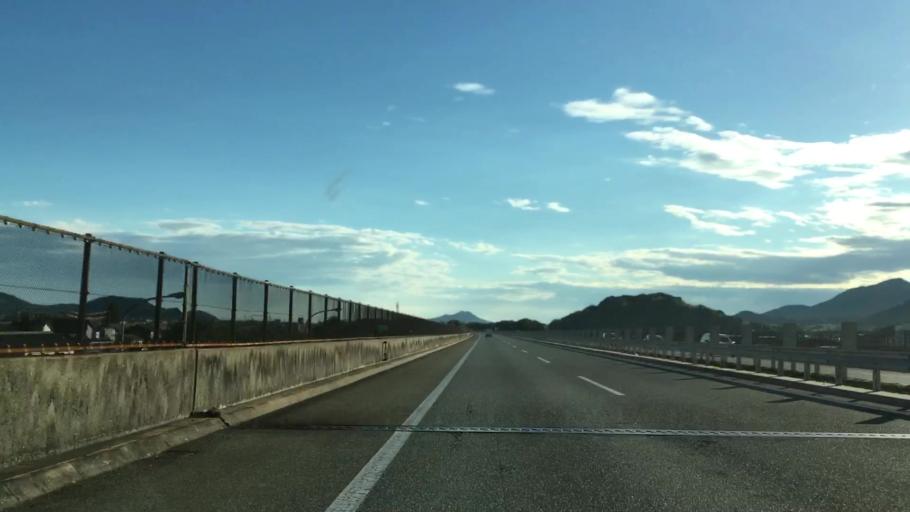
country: JP
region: Yamaguchi
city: Hofu
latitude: 34.0677
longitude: 131.5553
